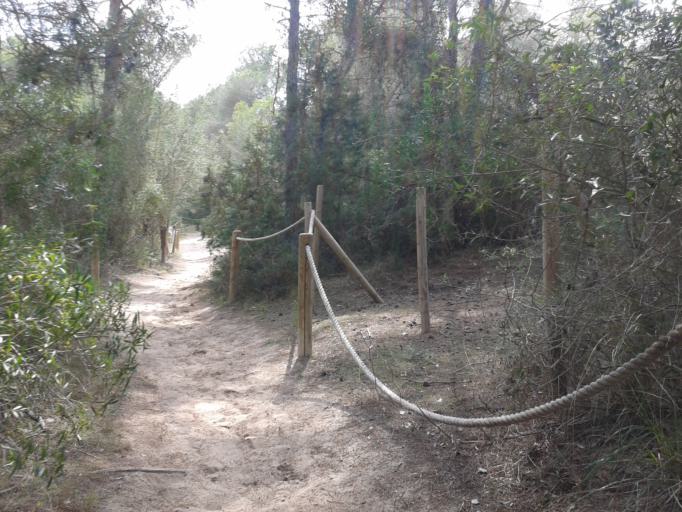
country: ES
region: Balearic Islands
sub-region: Illes Balears
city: Son Servera
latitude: 39.5824
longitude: 3.3838
